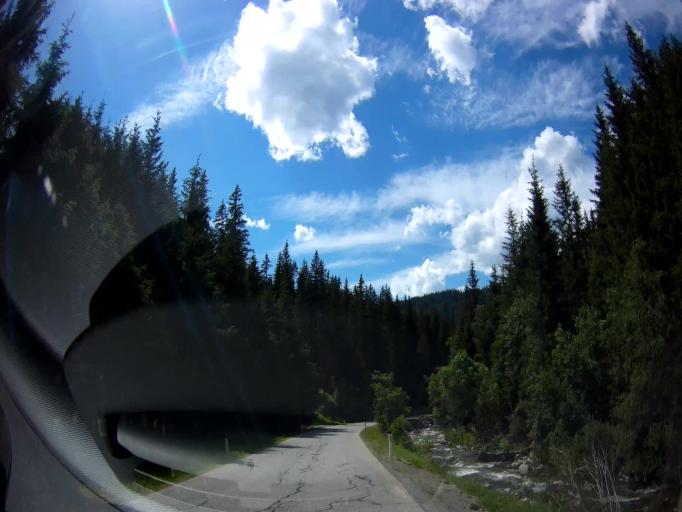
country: AT
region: Styria
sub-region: Politischer Bezirk Murau
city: Stadl an der Mur
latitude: 47.0133
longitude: 14.0079
